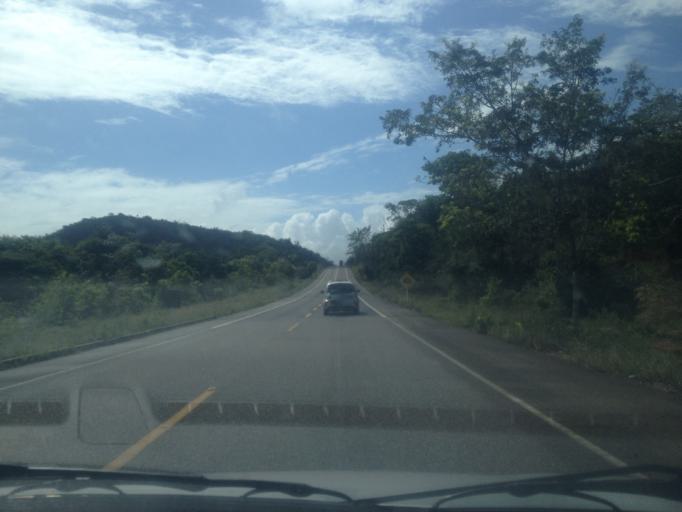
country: BR
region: Bahia
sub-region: Conde
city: Conde
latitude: -11.6914
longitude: -37.5698
